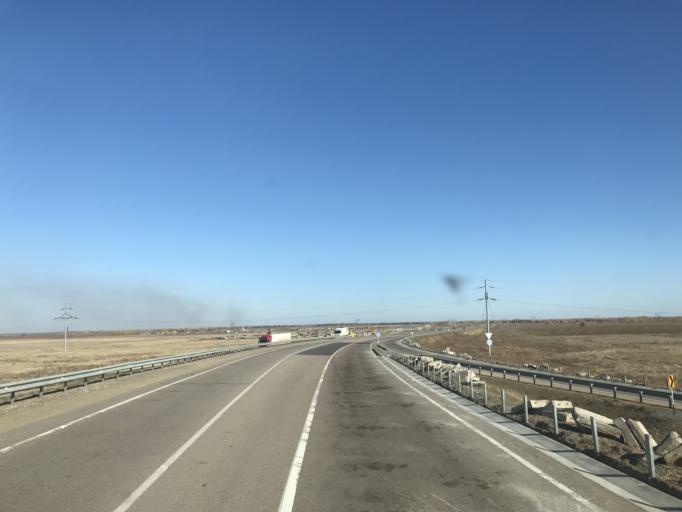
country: KZ
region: Pavlodar
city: Leninskiy
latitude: 52.1549
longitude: 76.8246
